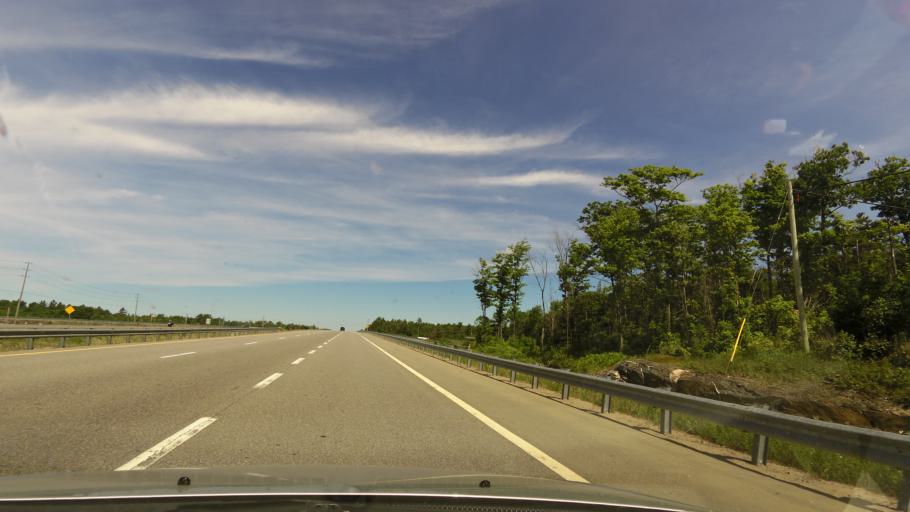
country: CA
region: Ontario
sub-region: Parry Sound District
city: Parry Sound
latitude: 45.3825
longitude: -80.0415
